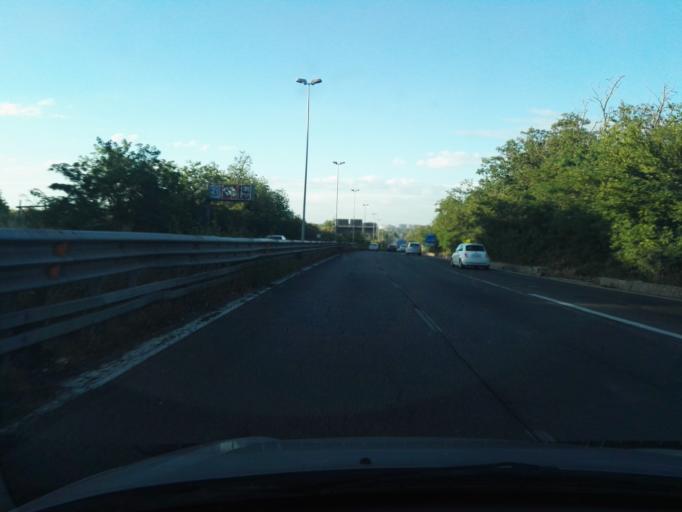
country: IT
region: Latium
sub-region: Citta metropolitana di Roma Capitale
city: Selcetta
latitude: 41.8036
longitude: 12.4544
